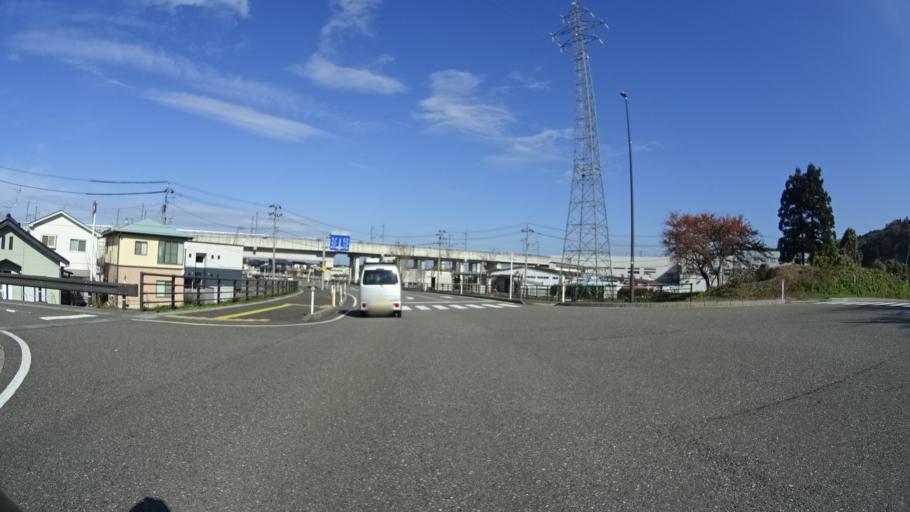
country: JP
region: Niigata
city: Itoigawa
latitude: 37.0496
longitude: 137.8942
